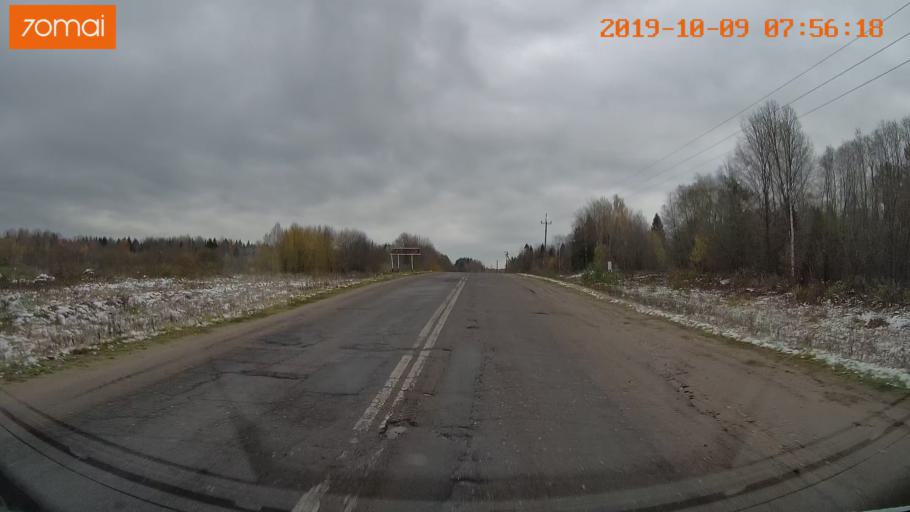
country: RU
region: Jaroslavl
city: Kukoboy
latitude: 58.6982
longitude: 39.9331
